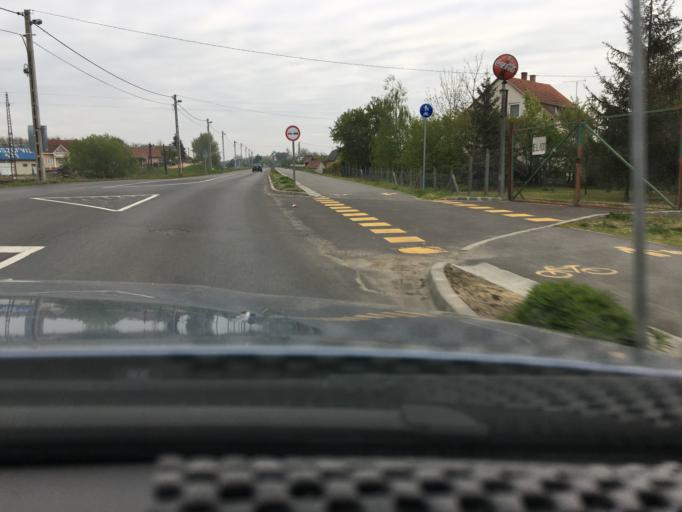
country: HU
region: Hajdu-Bihar
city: Hajdusamson
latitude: 47.6118
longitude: 21.7659
